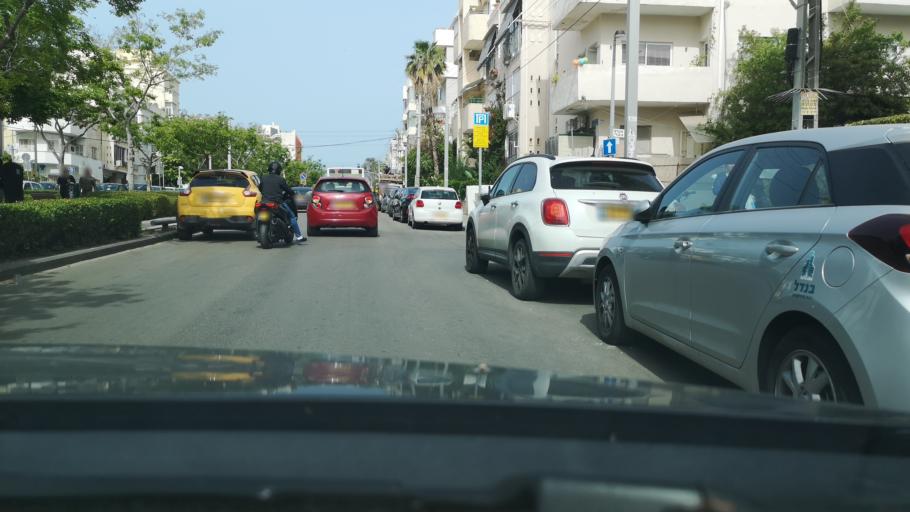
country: IL
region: Tel Aviv
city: Tel Aviv
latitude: 32.0923
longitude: 34.7778
